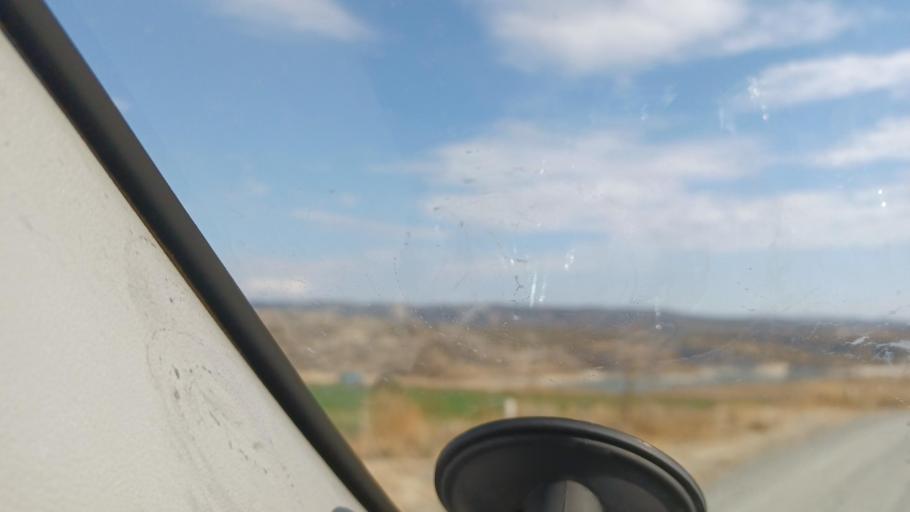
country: CY
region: Pafos
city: Mesogi
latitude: 34.7375
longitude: 32.5524
